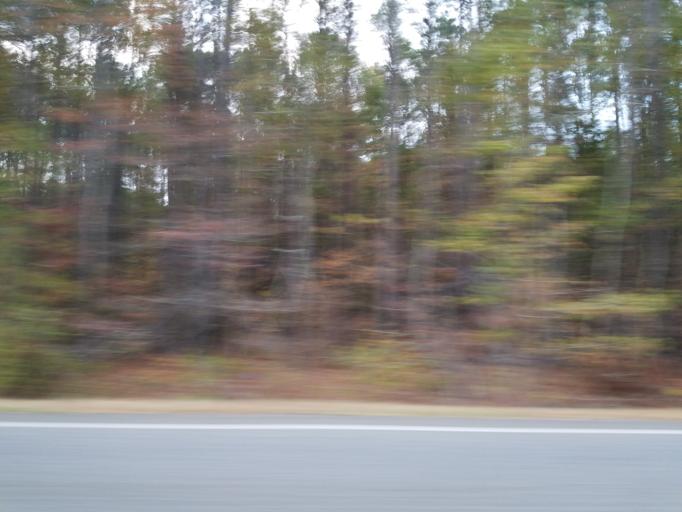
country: US
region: Georgia
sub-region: Murray County
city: Chatsworth
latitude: 34.5917
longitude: -84.6898
